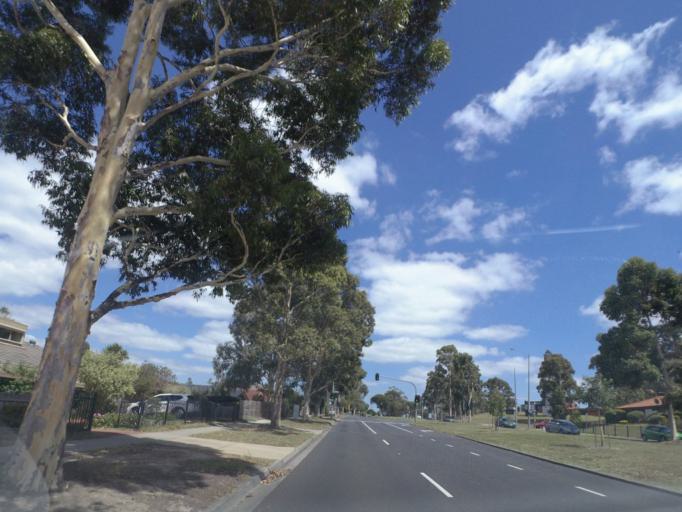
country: AU
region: Victoria
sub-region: Whittlesea
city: Mill Park
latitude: -37.6690
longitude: 145.0628
